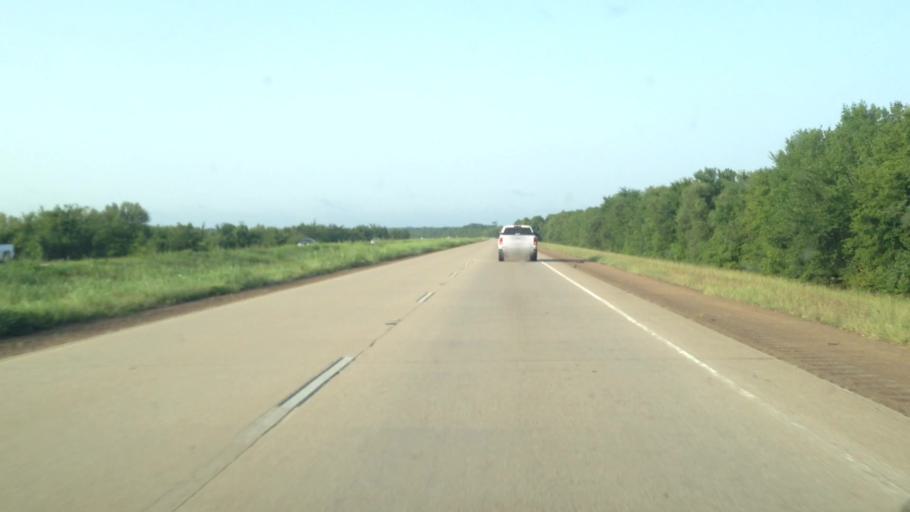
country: US
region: Louisiana
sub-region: Rapides Parish
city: Woodworth
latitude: 31.2106
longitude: -92.4715
